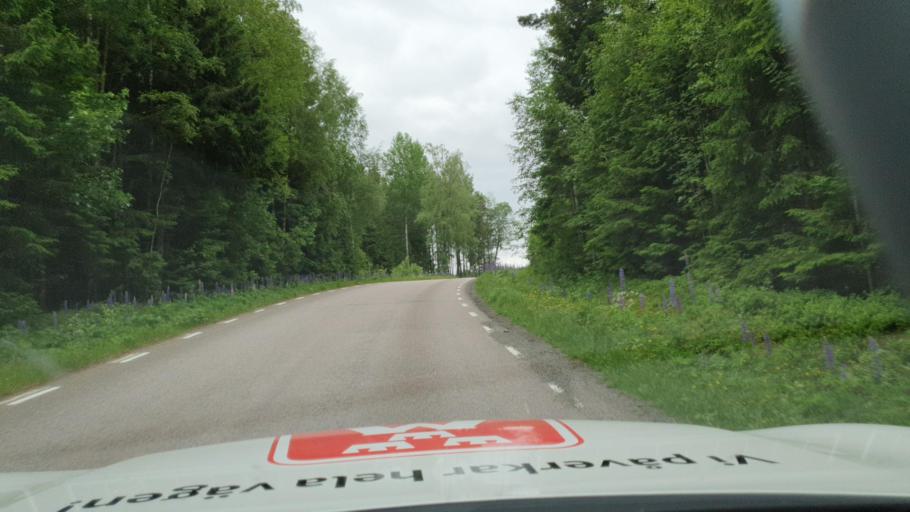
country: SE
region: Vaermland
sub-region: Sunne Kommun
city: Sunne
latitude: 59.7268
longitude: 13.2217
